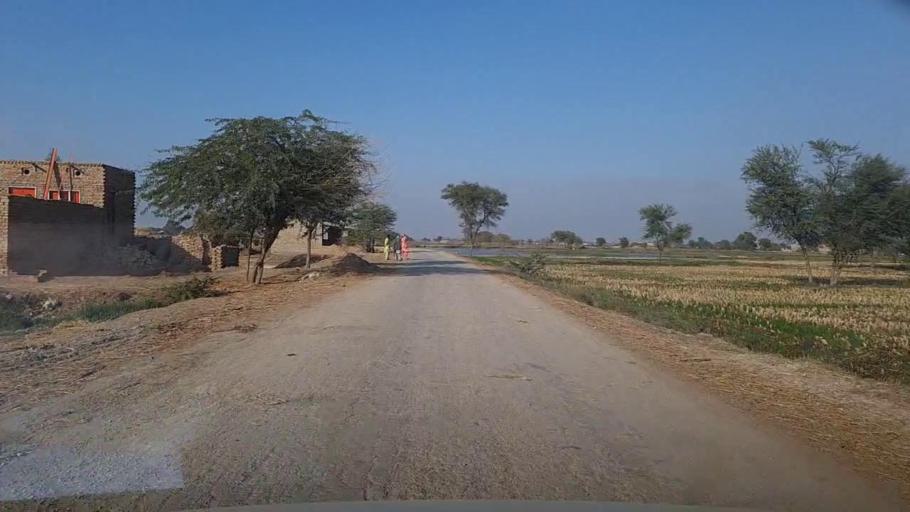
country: PK
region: Sindh
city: Phulji
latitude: 26.8605
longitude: 67.7946
